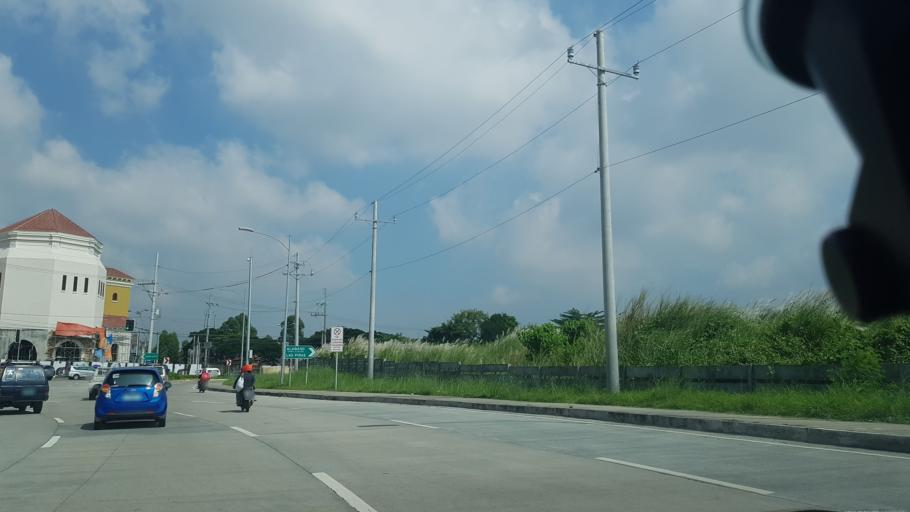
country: PH
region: Calabarzon
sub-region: Province of Laguna
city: San Pedro
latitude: 14.3759
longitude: 121.0137
